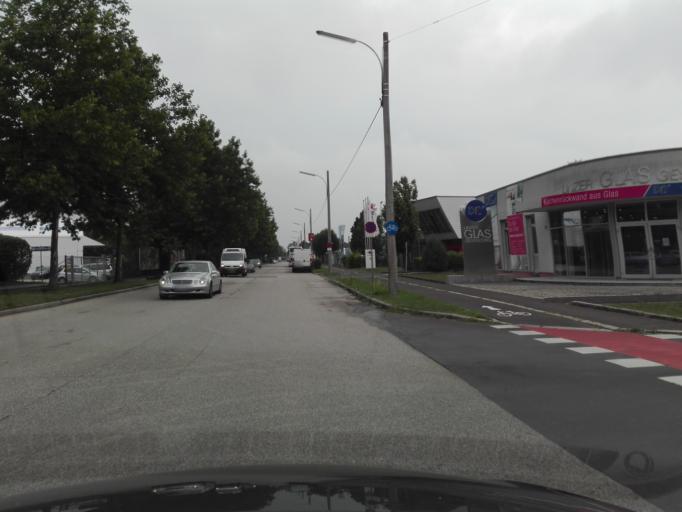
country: AT
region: Upper Austria
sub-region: Politischer Bezirk Linz-Land
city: Ansfelden
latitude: 48.2440
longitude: 14.2938
